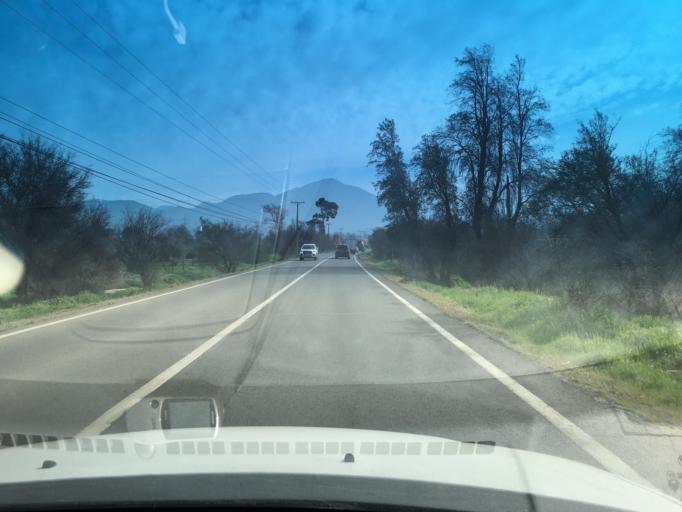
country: CL
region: Santiago Metropolitan
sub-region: Provincia de Chacabuco
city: Lampa
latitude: -33.1243
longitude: -70.9240
